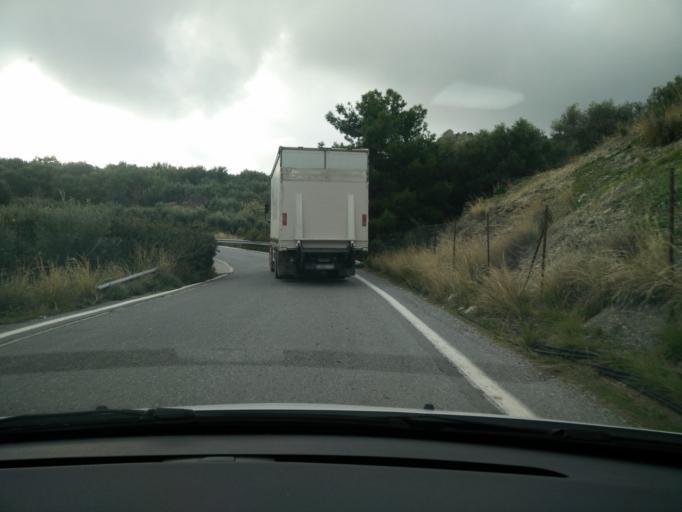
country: GR
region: Crete
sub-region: Nomos Lasithiou
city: Gra Liyia
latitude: 35.0256
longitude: 25.5634
